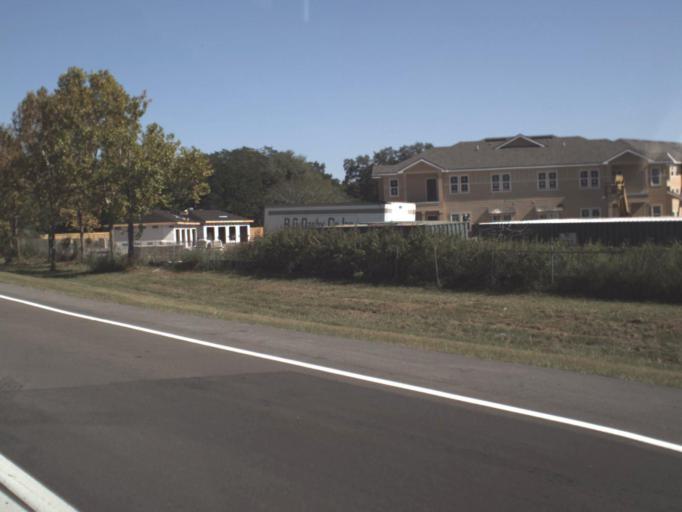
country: US
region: Florida
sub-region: Hillsborough County
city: Citrus Park
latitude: 28.0615
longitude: -82.5695
